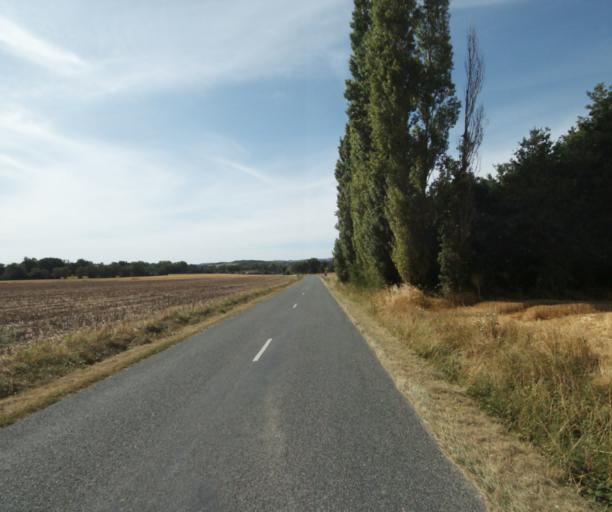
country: FR
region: Midi-Pyrenees
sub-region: Departement du Tarn
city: Soual
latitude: 43.5132
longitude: 2.0827
